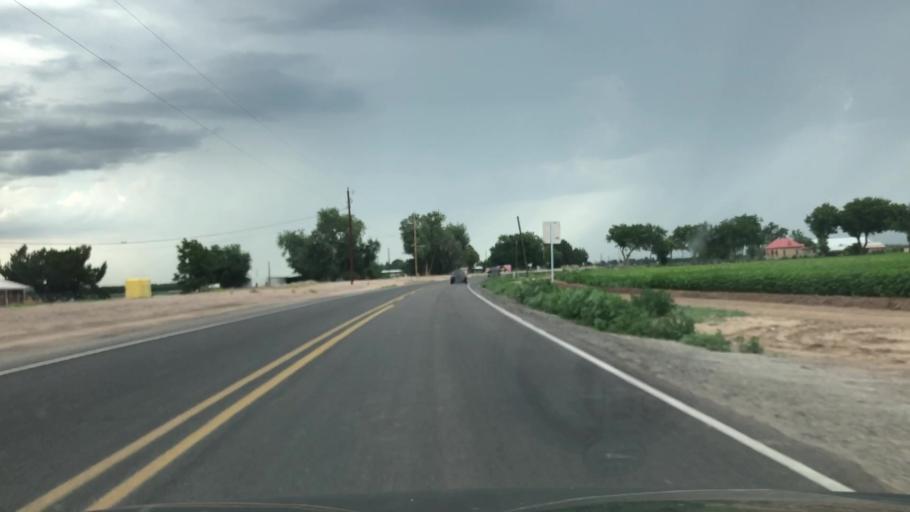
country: US
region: New Mexico
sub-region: Dona Ana County
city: Berino
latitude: 32.0265
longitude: -106.6720
